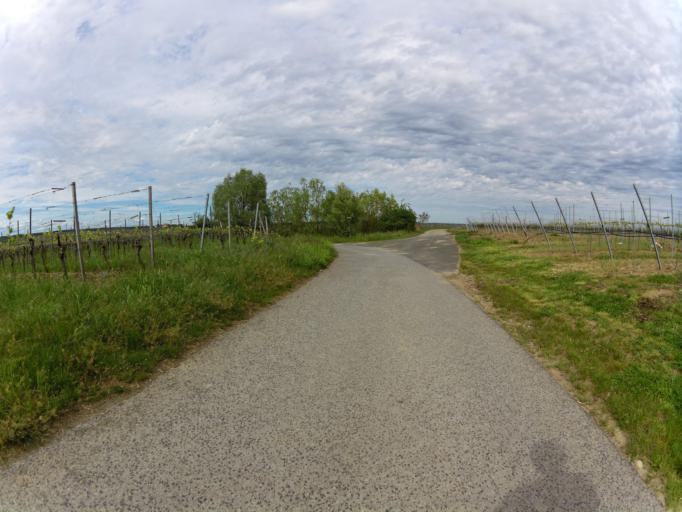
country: DE
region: Bavaria
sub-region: Regierungsbezirk Unterfranken
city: Nordheim
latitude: 49.8501
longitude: 10.1893
